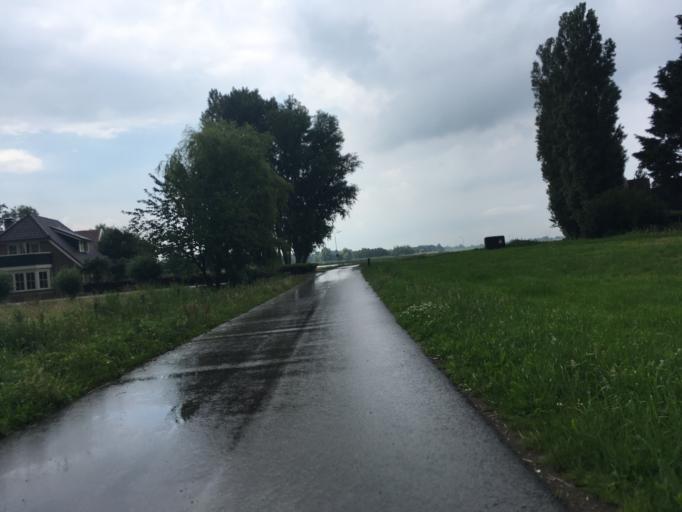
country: NL
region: North Holland
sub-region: Gemeente Velsen
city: Velsen-Zuid
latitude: 52.4164
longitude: 4.7285
